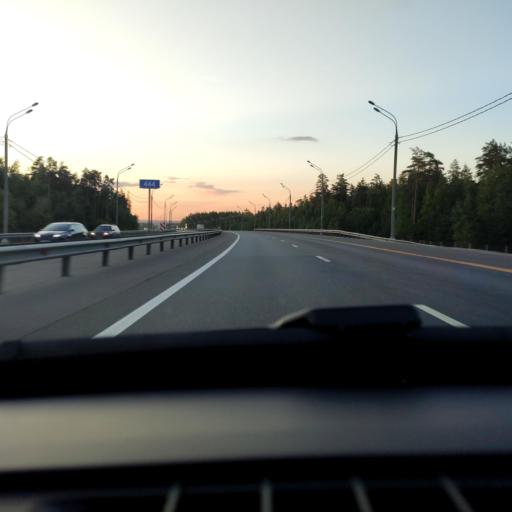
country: RU
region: Lipetsk
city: Khlevnoye
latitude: 52.2544
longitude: 39.0658
